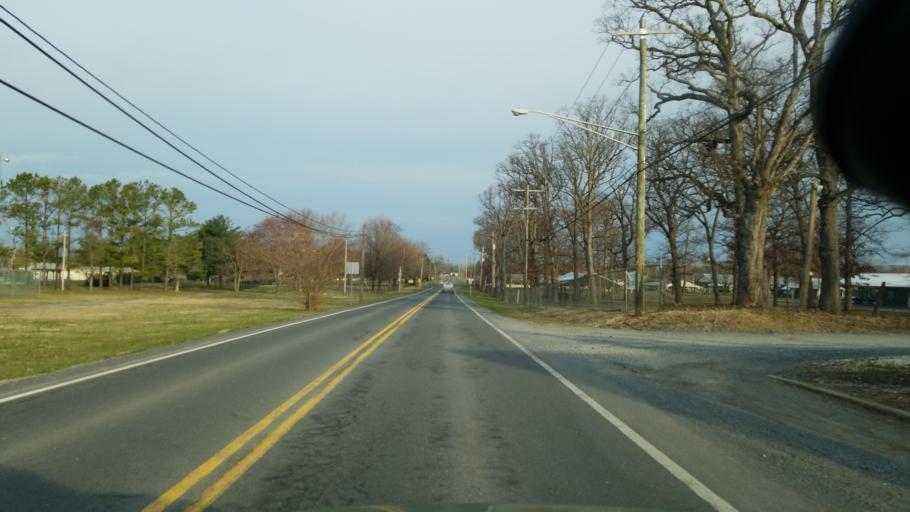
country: US
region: Virginia
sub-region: Clarke County
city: Berryville
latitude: 39.1629
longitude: -77.9985
